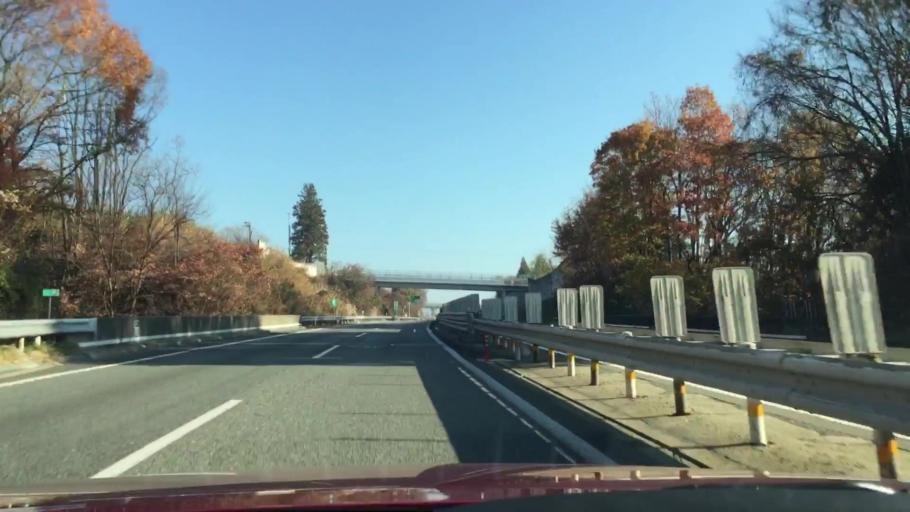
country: JP
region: Nagano
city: Iida
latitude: 35.5401
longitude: 137.8381
